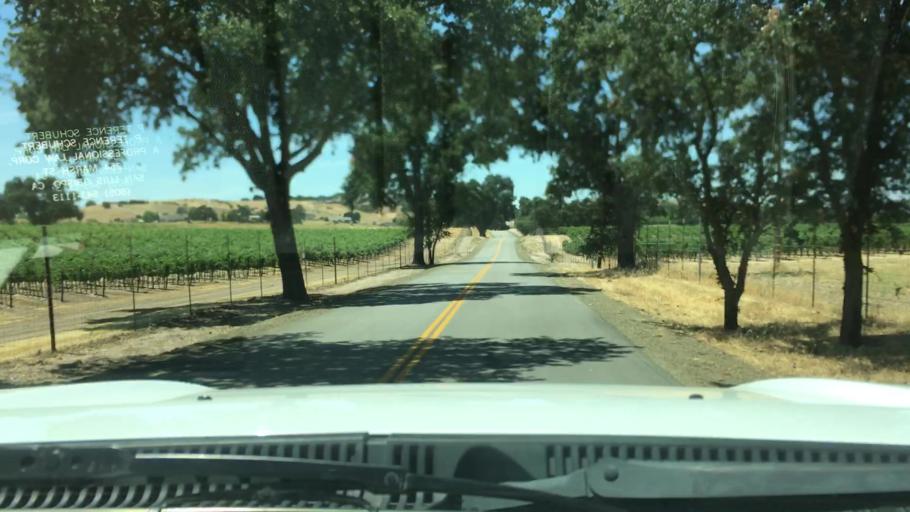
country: US
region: California
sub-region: San Luis Obispo County
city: Paso Robles
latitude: 35.5753
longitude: -120.6272
